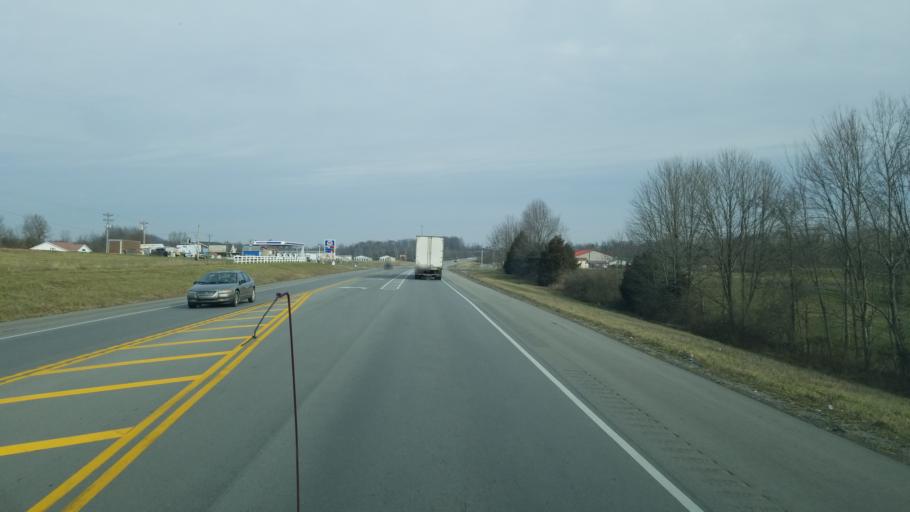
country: US
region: Kentucky
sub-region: Boyle County
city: Junction City
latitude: 37.5608
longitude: -84.7985
